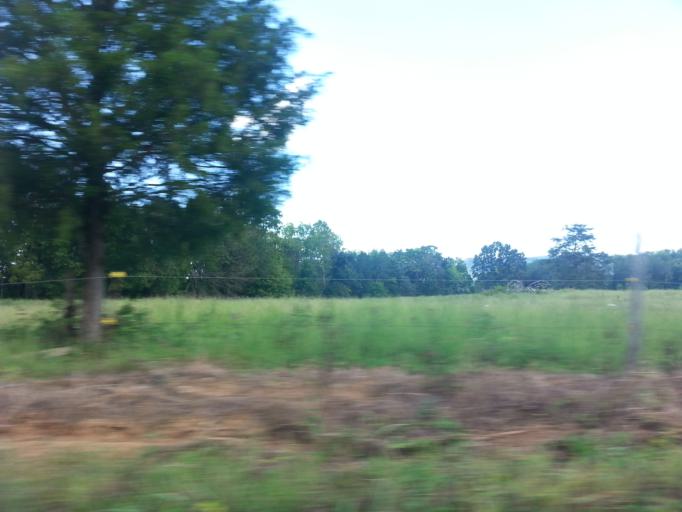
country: US
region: Tennessee
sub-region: Grainger County
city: Blaine
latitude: 36.1390
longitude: -83.7295
